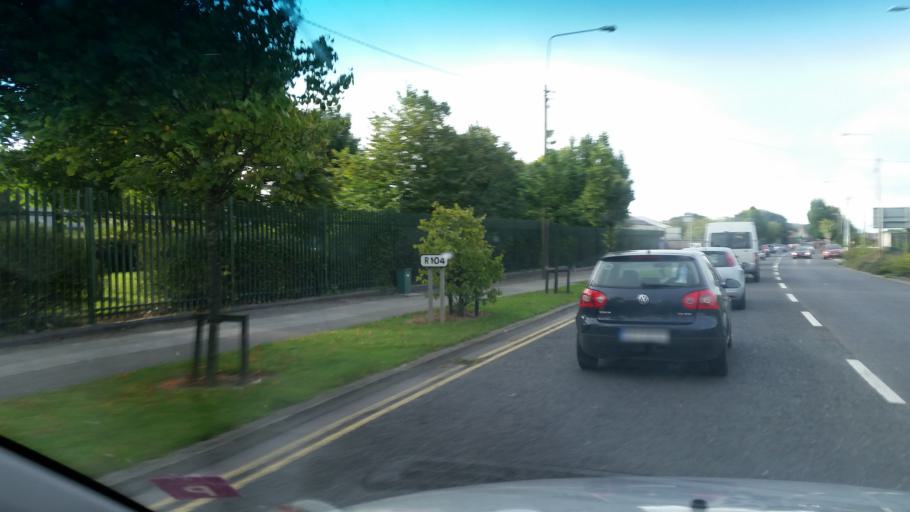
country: IE
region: Leinster
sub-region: Dublin City
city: Finglas
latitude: 53.4015
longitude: -6.3028
